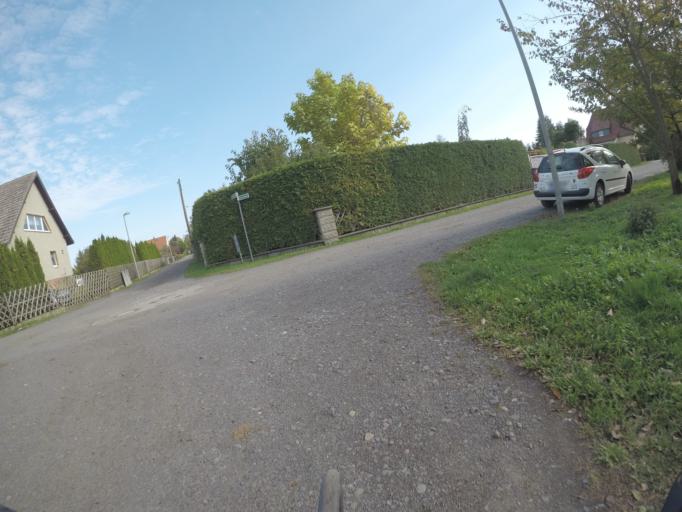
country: DE
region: Brandenburg
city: Leegebruch
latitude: 52.7483
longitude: 13.2031
